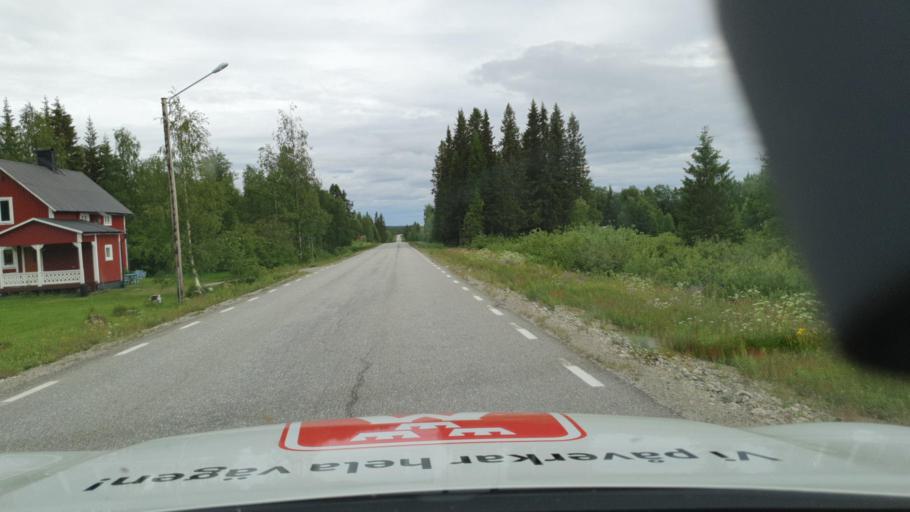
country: SE
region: Vaesterbotten
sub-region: Lycksele Kommun
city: Soderfors
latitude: 64.3567
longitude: 18.1227
